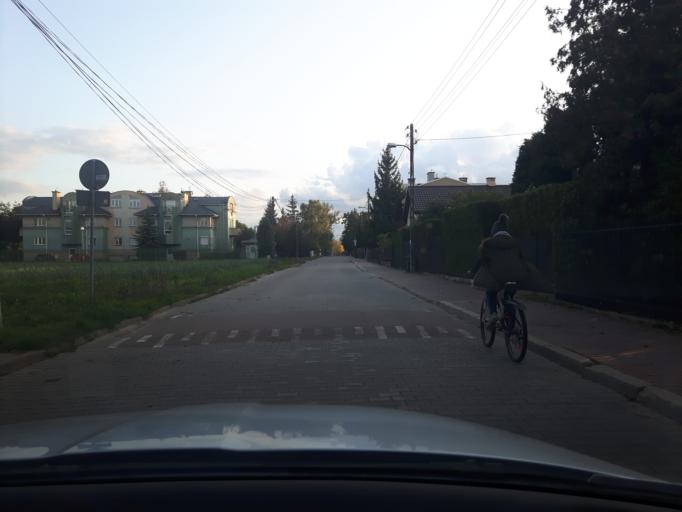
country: PL
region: Masovian Voivodeship
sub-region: Warszawa
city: Ursynow
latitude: 52.1499
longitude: 21.0222
